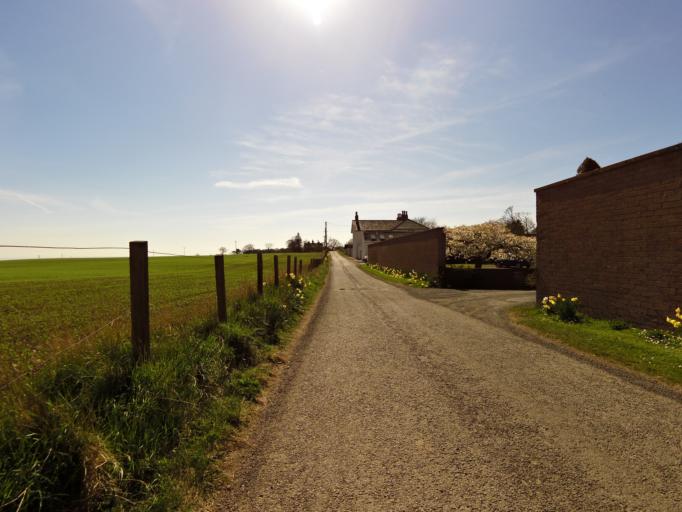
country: GB
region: Scotland
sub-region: Angus
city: Montrose
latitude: 56.6959
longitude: -2.4610
